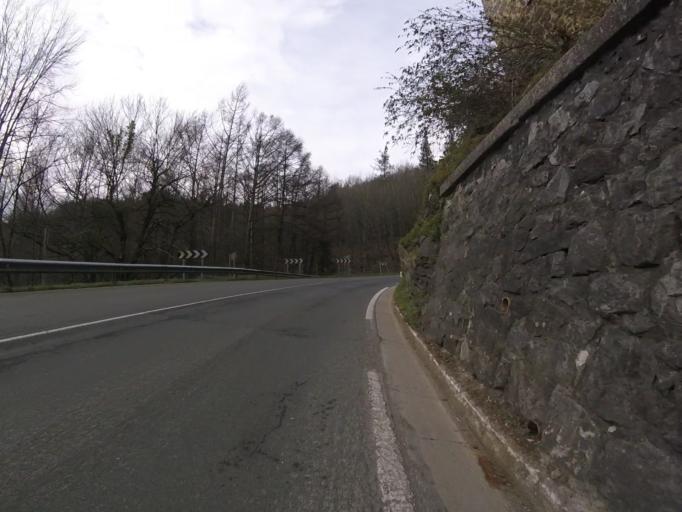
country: ES
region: Basque Country
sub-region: Provincia de Guipuzcoa
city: Albiztur
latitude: 43.1251
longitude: -2.1563
